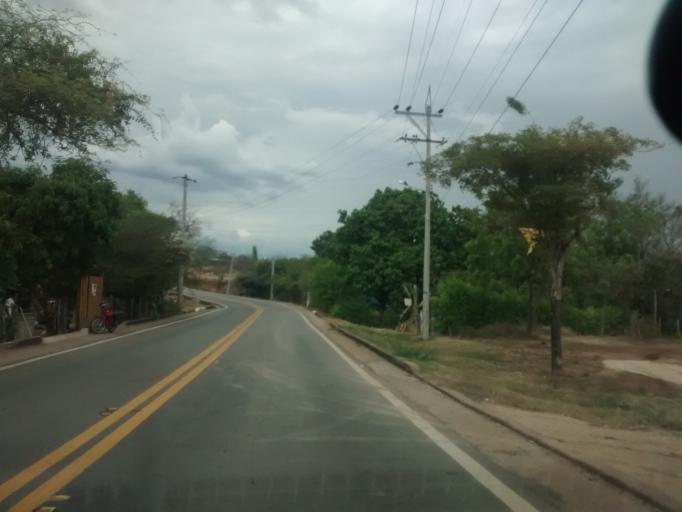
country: CO
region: Cundinamarca
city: Tocaima
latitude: 4.4342
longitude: -74.6836
